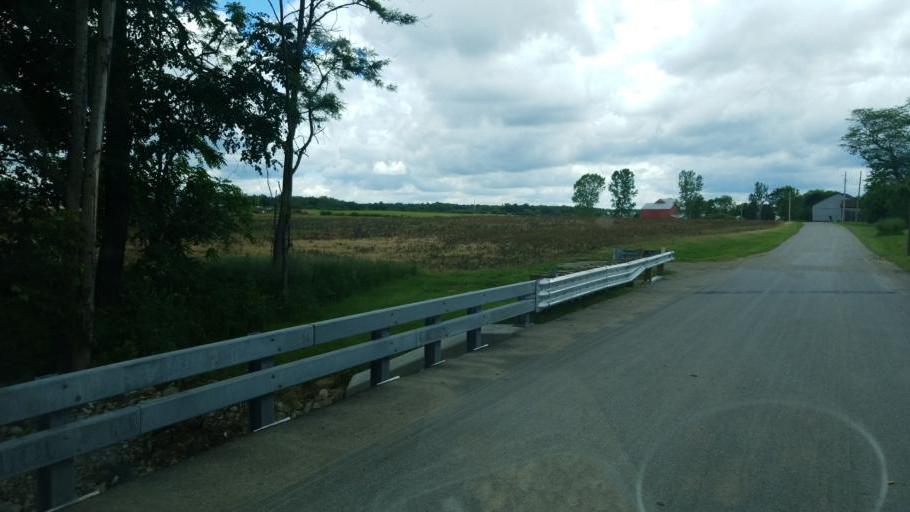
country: US
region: Ohio
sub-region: Richland County
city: Lexington
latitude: 40.6133
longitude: -82.6291
